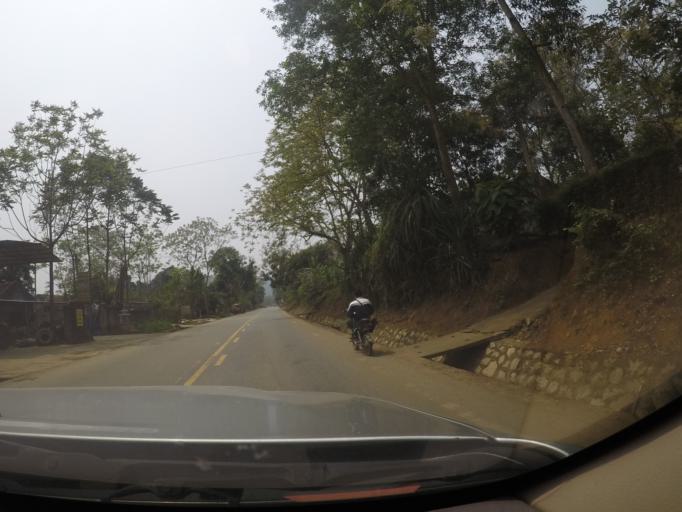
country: VN
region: Thanh Hoa
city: Thi Tran Cam Thuy
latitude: 20.1709
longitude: 105.4783
